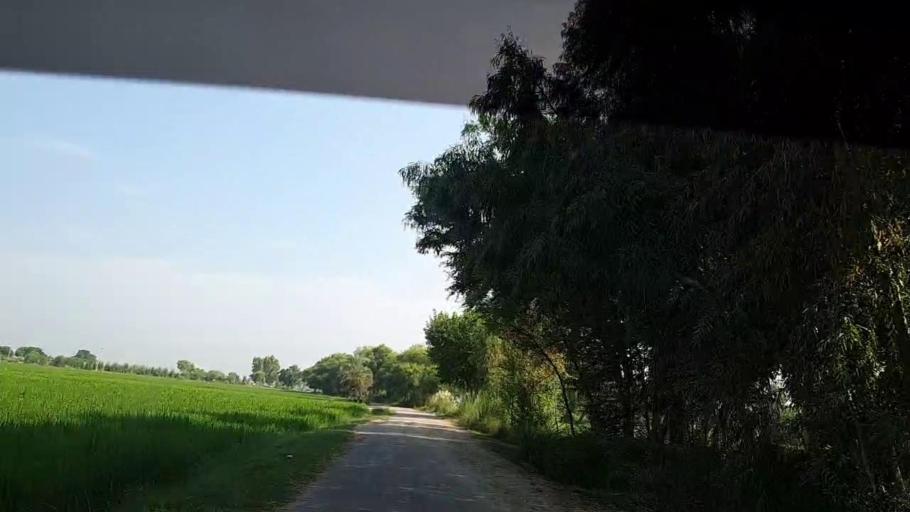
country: PK
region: Sindh
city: Shikarpur
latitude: 28.0937
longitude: 68.6762
